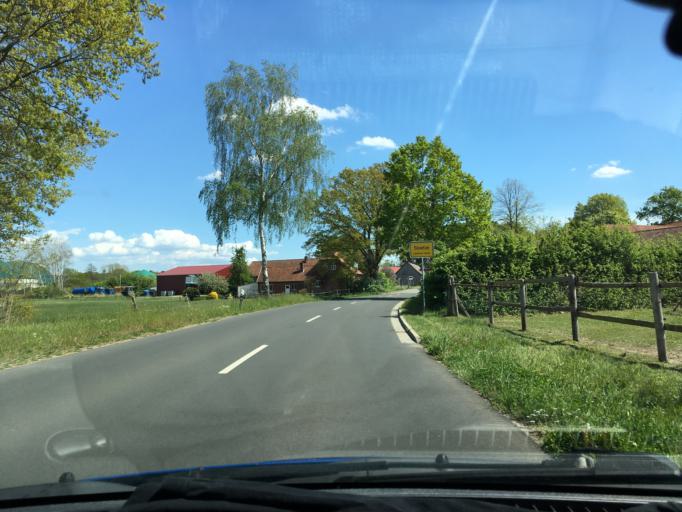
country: DE
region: Lower Saxony
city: Stoetze
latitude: 53.0701
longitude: 10.7805
